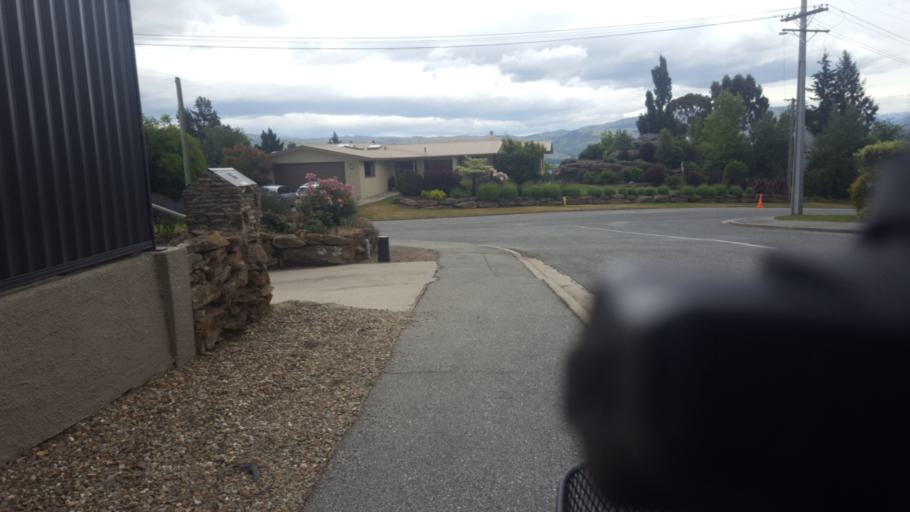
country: NZ
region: Otago
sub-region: Queenstown-Lakes District
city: Wanaka
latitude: -45.2628
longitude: 169.3788
